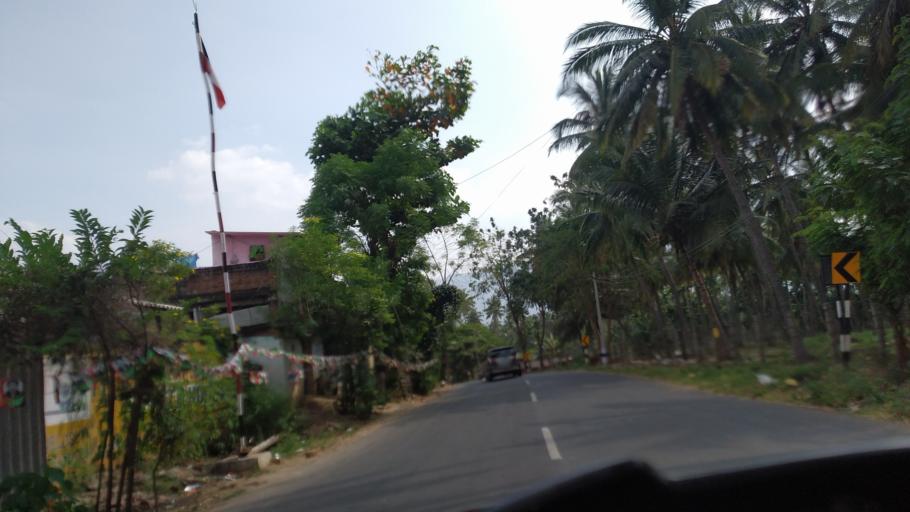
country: IN
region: Tamil Nadu
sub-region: Coimbatore
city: Perur
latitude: 10.9524
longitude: 76.7635
